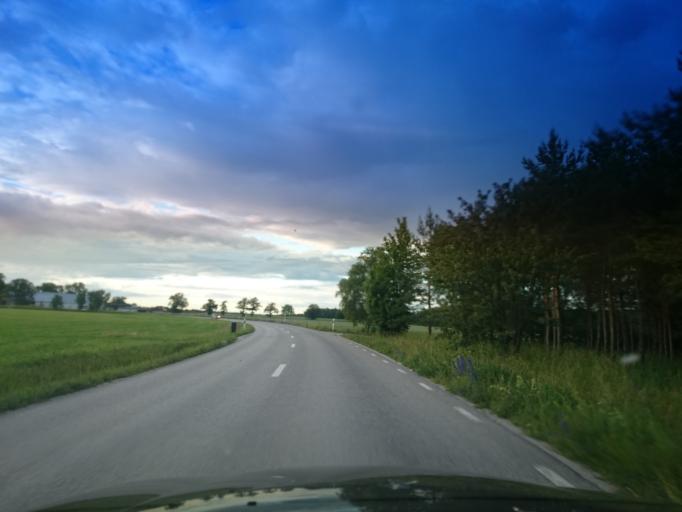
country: SE
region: Gotland
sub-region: Gotland
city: Vibble
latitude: 57.4999
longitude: 18.3721
